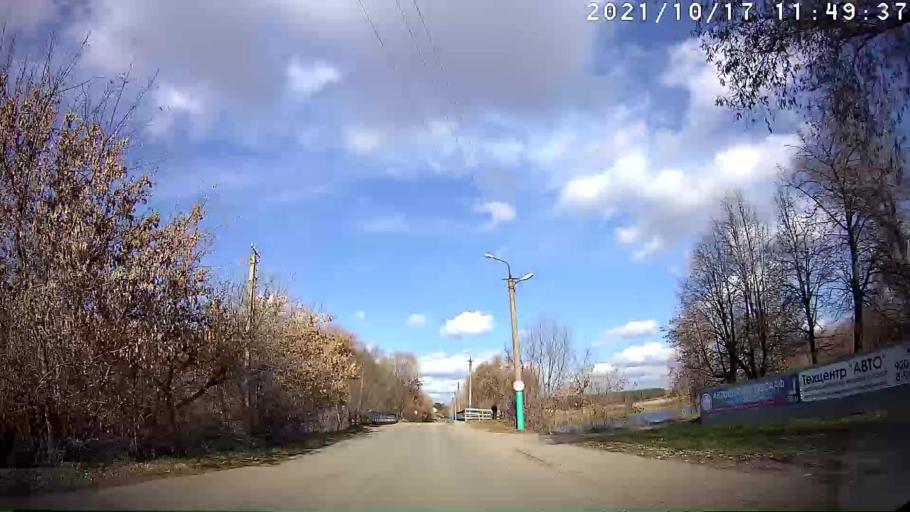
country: RU
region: Mariy-El
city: Kuzhener
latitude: 57.0073
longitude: 48.7367
